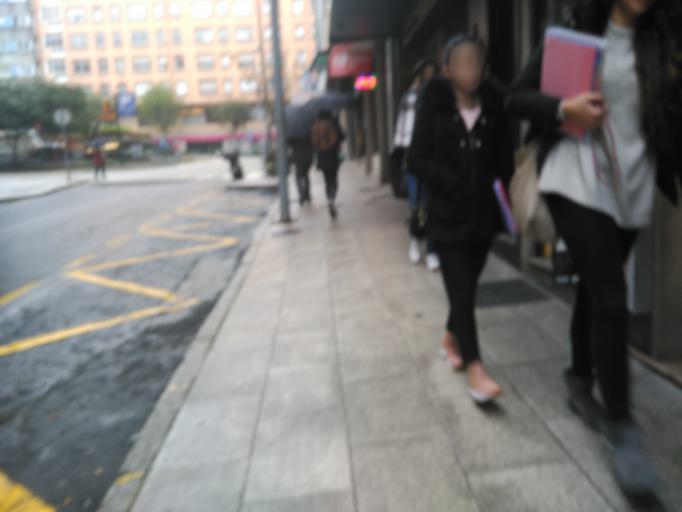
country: ES
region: Galicia
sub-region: Provincia da Coruna
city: Santiago de Compostela
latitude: 42.8735
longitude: -8.5516
